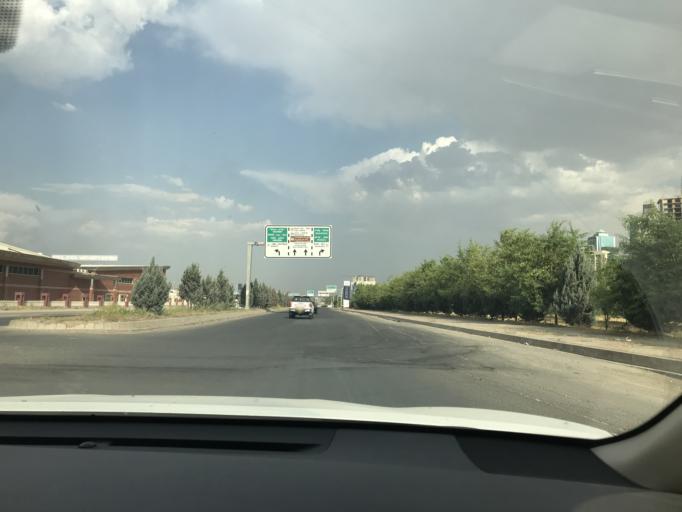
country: IQ
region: Arbil
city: Erbil
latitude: 36.2055
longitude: 43.9637
